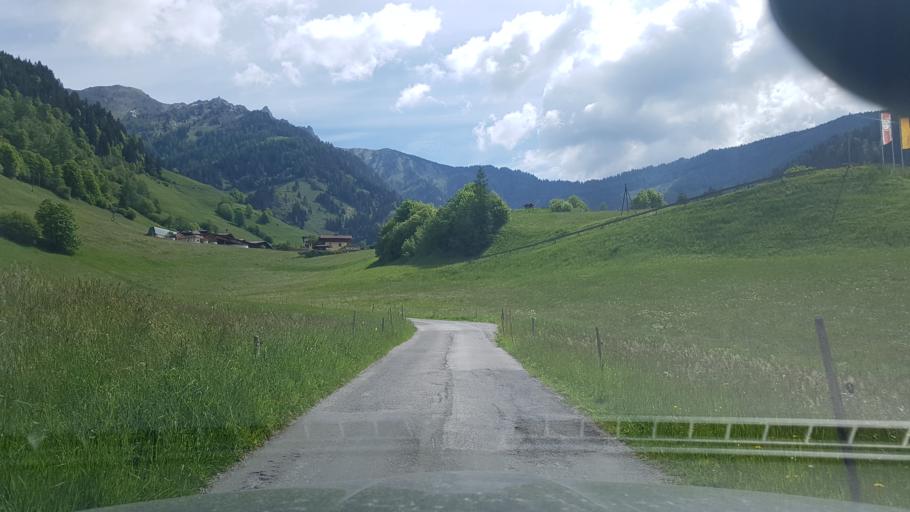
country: AT
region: Salzburg
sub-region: Politischer Bezirk Sankt Johann im Pongau
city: Dorfgastein
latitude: 47.2495
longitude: 13.1127
